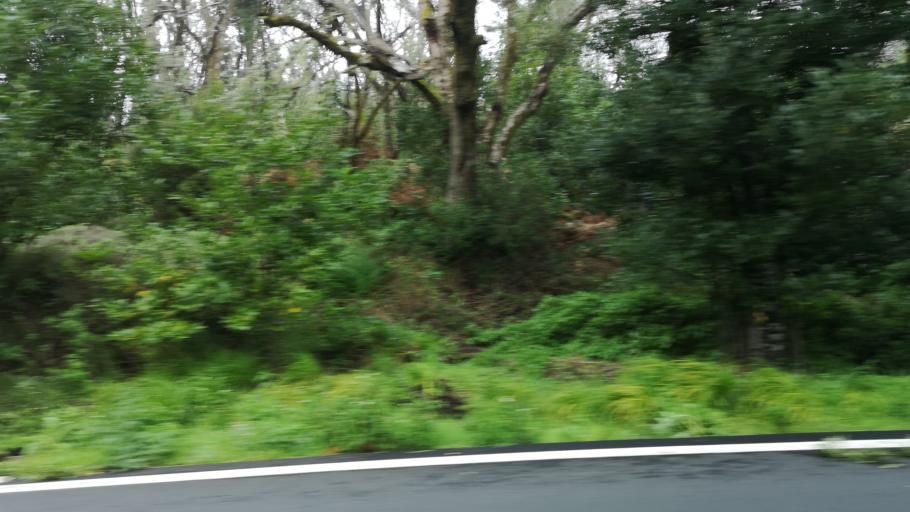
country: ES
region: Canary Islands
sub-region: Provincia de Santa Cruz de Tenerife
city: Vallehermosa
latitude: 28.1307
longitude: -17.2749
